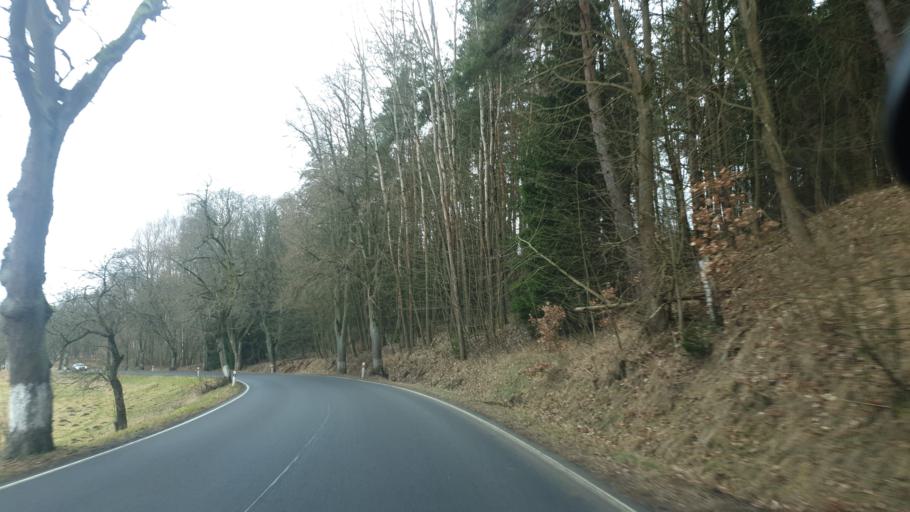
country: CZ
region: Karlovarsky
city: As
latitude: 50.2506
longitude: 12.1946
